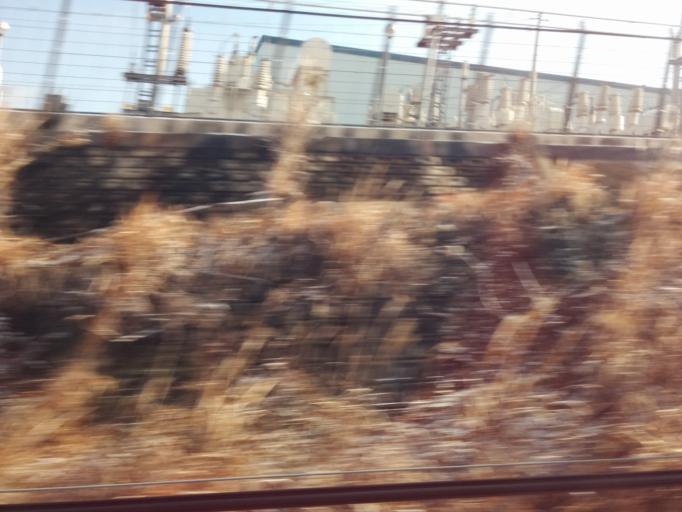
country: JP
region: Aichi
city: Obu
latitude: 35.0514
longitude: 136.9516
